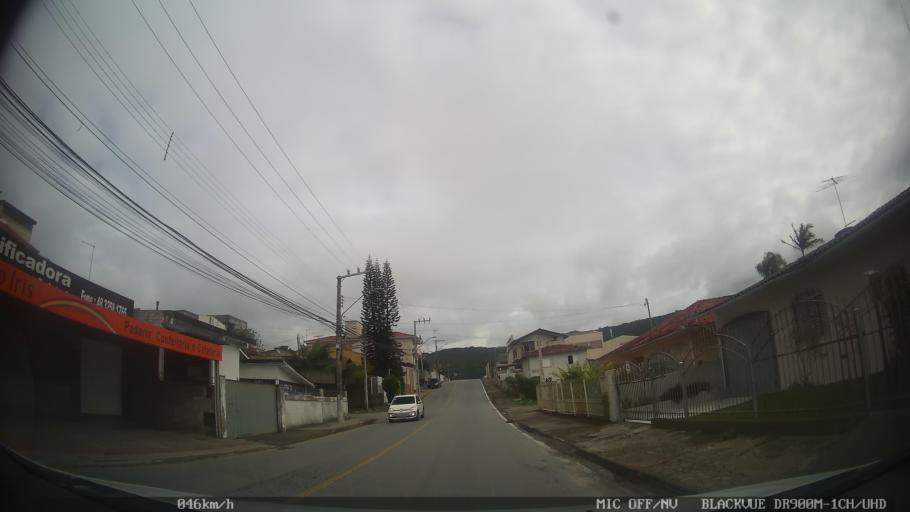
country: BR
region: Santa Catarina
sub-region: Biguacu
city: Biguacu
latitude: -27.5438
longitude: -48.6389
